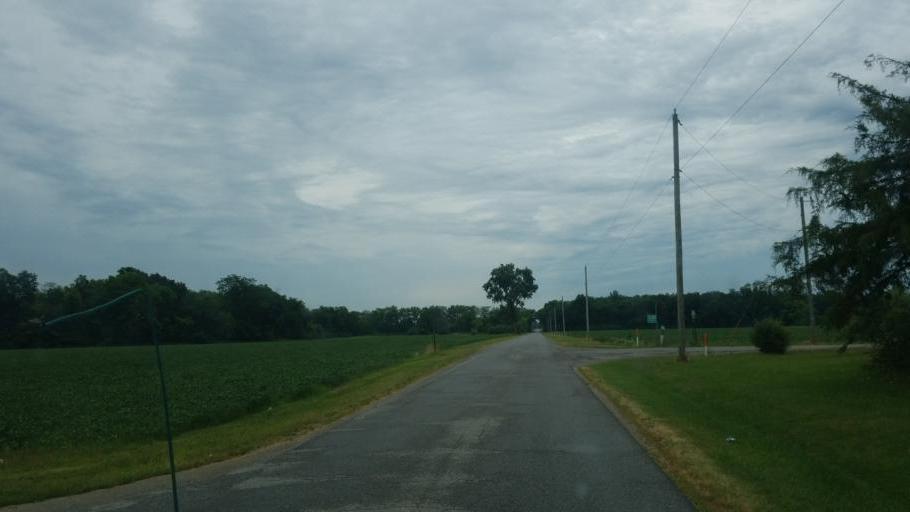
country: US
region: Ohio
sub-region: Paulding County
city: Antwerp
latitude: 41.2417
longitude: -84.6892
